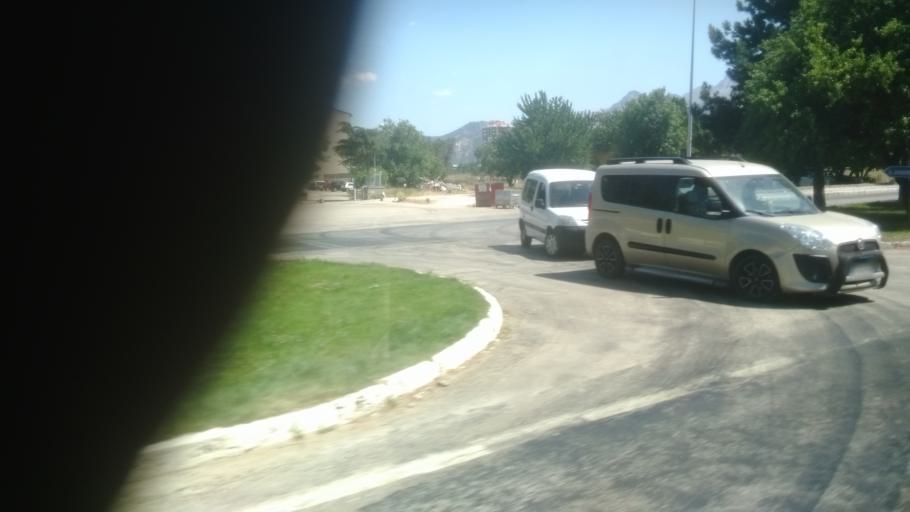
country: TR
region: Isparta
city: Isparta
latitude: 37.7826
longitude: 30.5669
